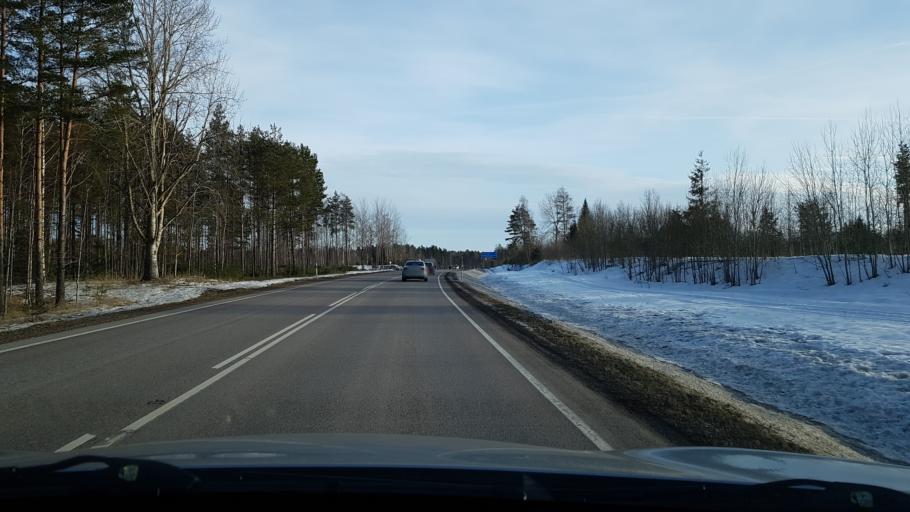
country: EE
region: Tartu
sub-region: Puhja vald
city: Puhja
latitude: 58.4110
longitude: 26.0729
